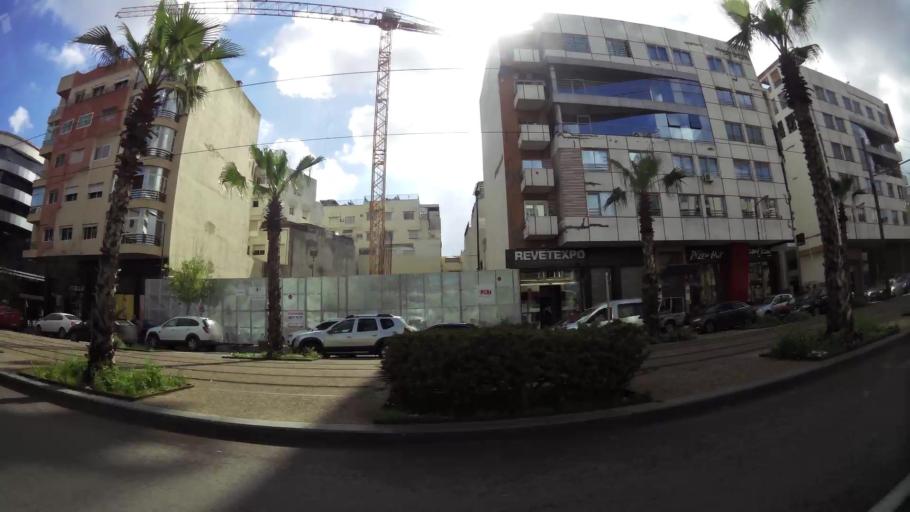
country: MA
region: Grand Casablanca
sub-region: Casablanca
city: Casablanca
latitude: 33.5681
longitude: -7.6262
